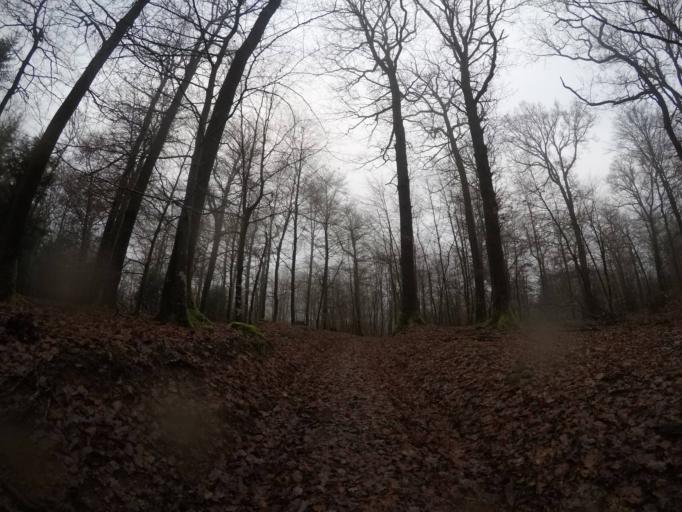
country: BE
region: Wallonia
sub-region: Province du Luxembourg
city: Fauvillers
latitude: 49.8111
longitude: 5.6185
